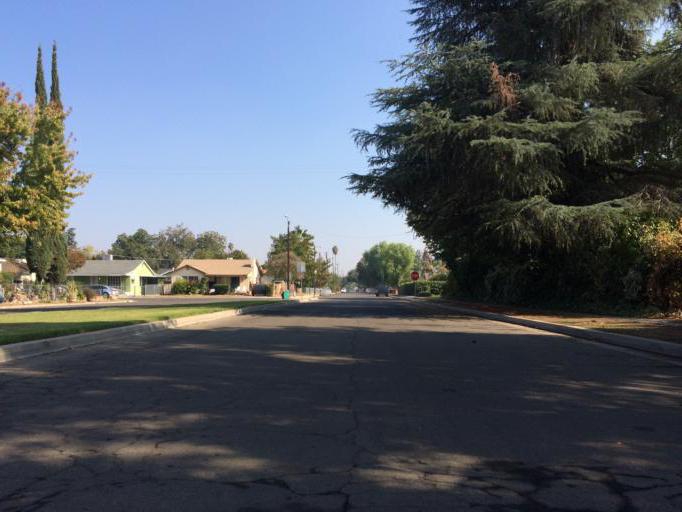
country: US
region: California
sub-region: Fresno County
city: Fresno
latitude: 36.7468
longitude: -119.7416
